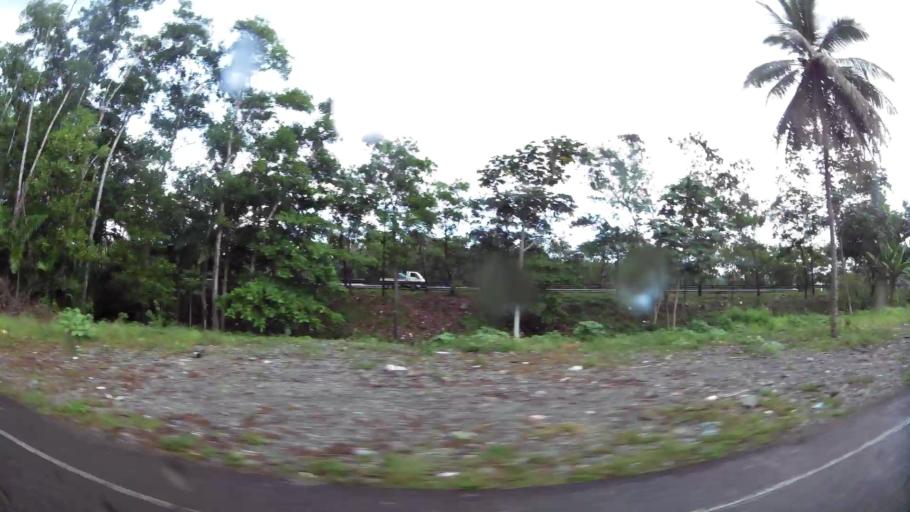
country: DO
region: Monsenor Nouel
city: Bonao
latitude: 18.9375
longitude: -70.3915
